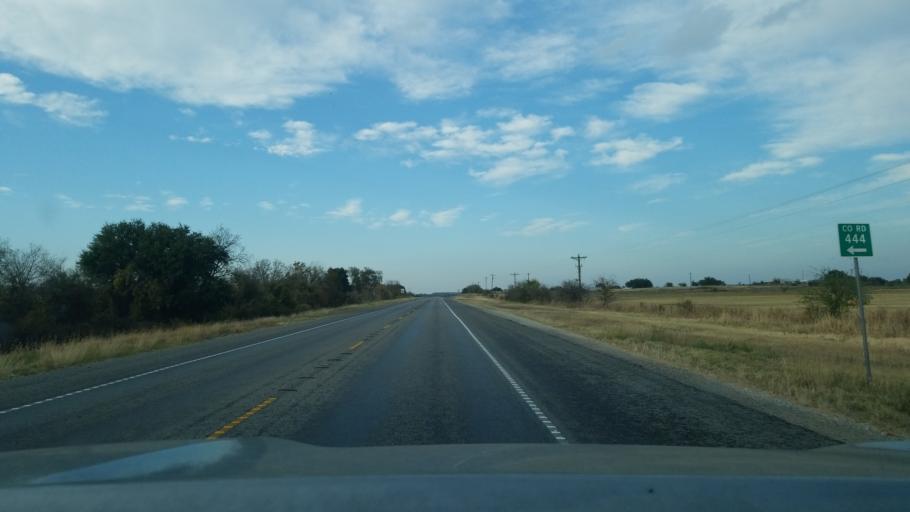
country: US
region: Texas
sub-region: Brown County
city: Lake Brownwood
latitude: 31.9855
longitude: -98.9207
